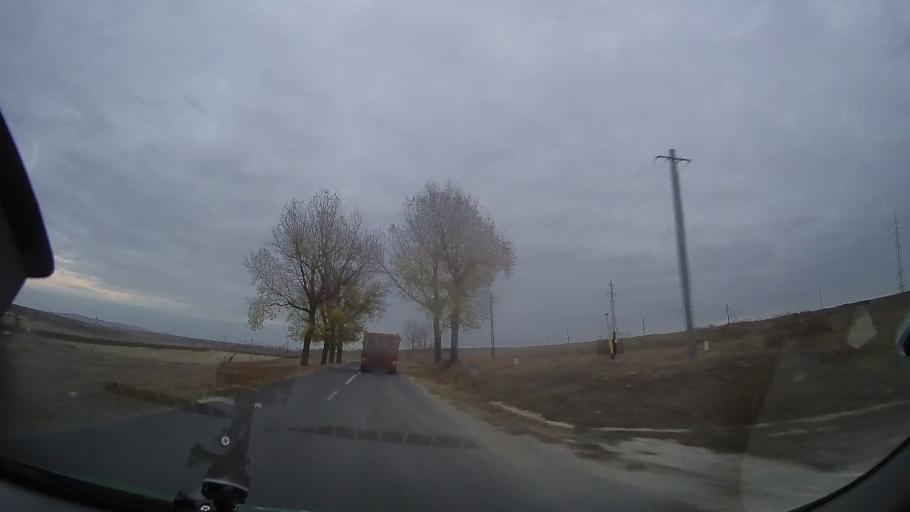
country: RO
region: Tulcea
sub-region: Comuna Mihai Bravu
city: Mihai Bravu
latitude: 44.9593
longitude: 28.6464
